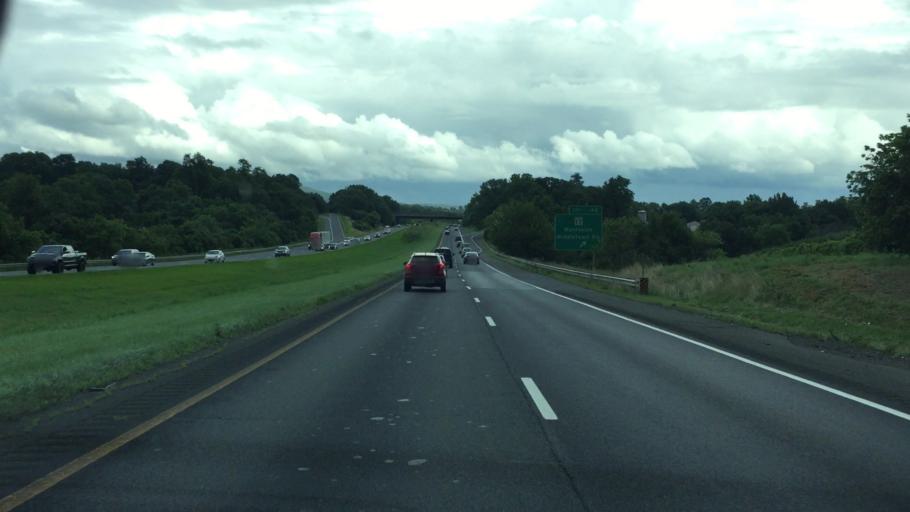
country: US
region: Maryland
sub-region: Frederick County
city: Myersville
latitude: 39.5001
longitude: -77.5740
